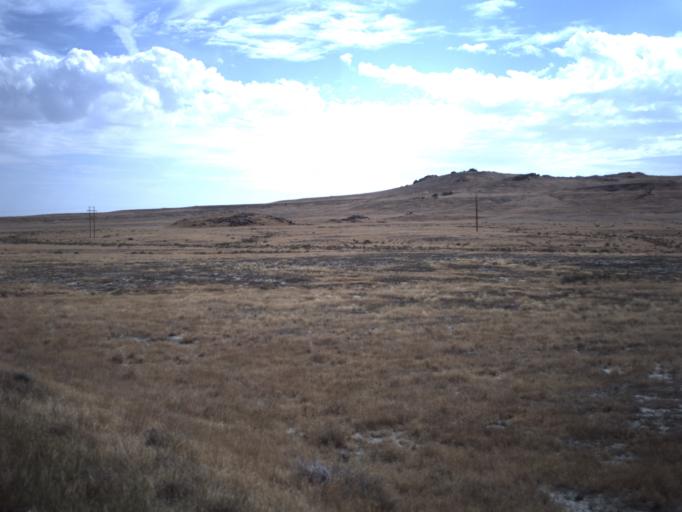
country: US
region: Utah
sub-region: Tooele County
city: Wendover
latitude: 41.4102
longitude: -113.9297
